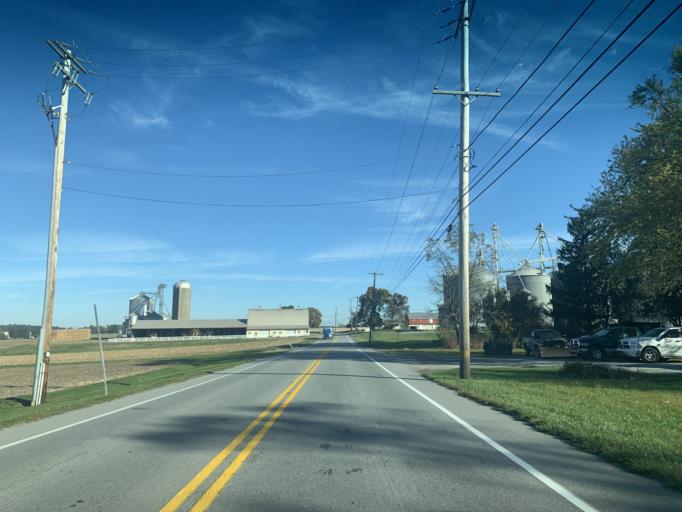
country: US
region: Pennsylvania
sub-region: Chester County
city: Parkesburg
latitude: 39.9071
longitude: -75.9102
